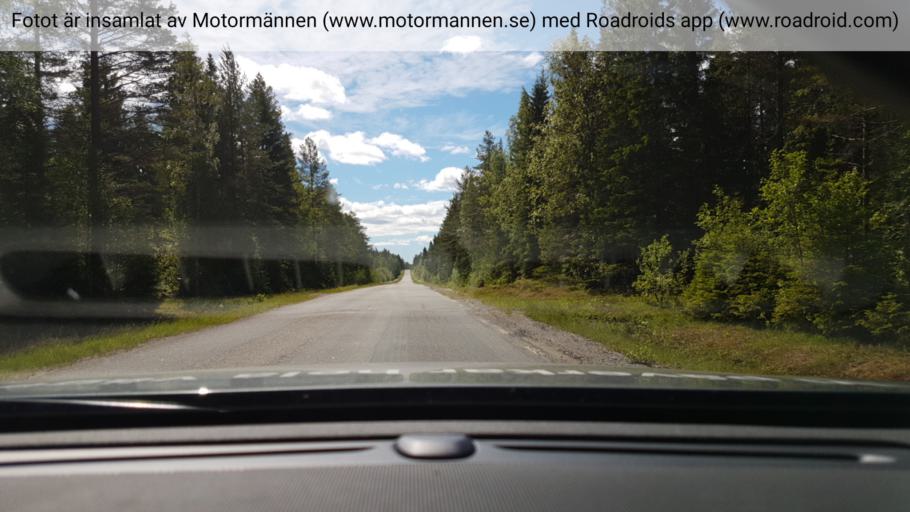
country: SE
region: Vaesterbotten
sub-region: Skelleftea Kommun
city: Burea
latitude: 64.4321
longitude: 21.3537
